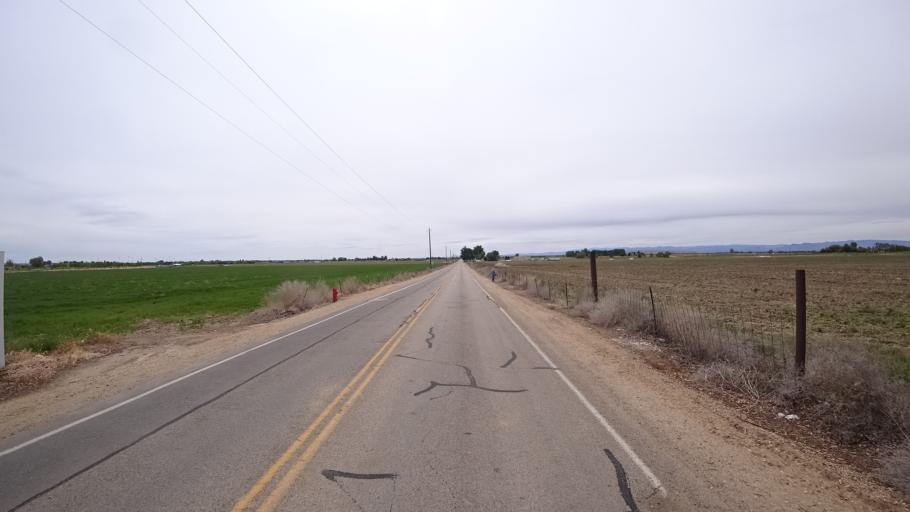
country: US
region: Idaho
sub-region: Ada County
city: Meridian
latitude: 43.5498
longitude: -116.3747
